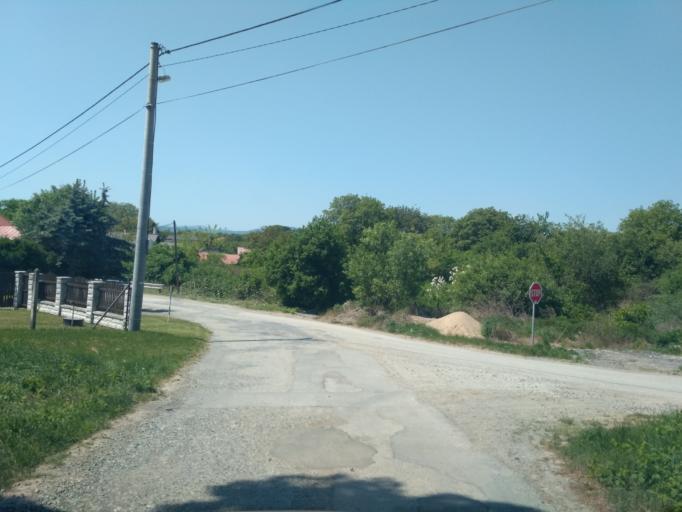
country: SK
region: Kosicky
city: Kosice
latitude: 48.7931
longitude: 21.3570
